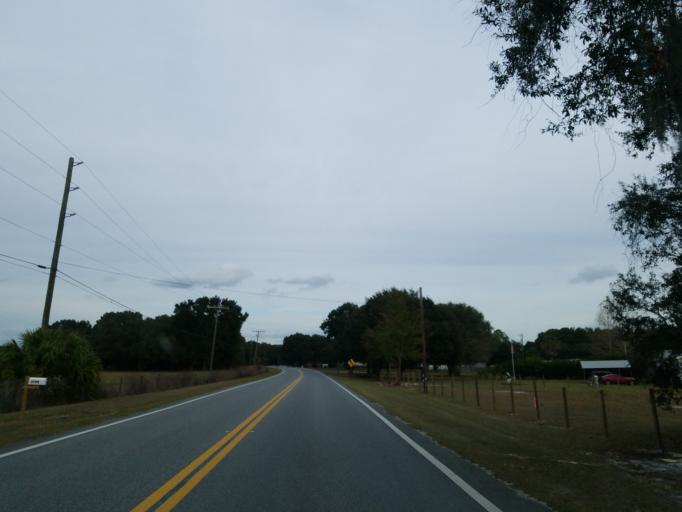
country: US
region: Florida
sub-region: Sumter County
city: Bushnell
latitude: 28.6087
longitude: -82.1510
